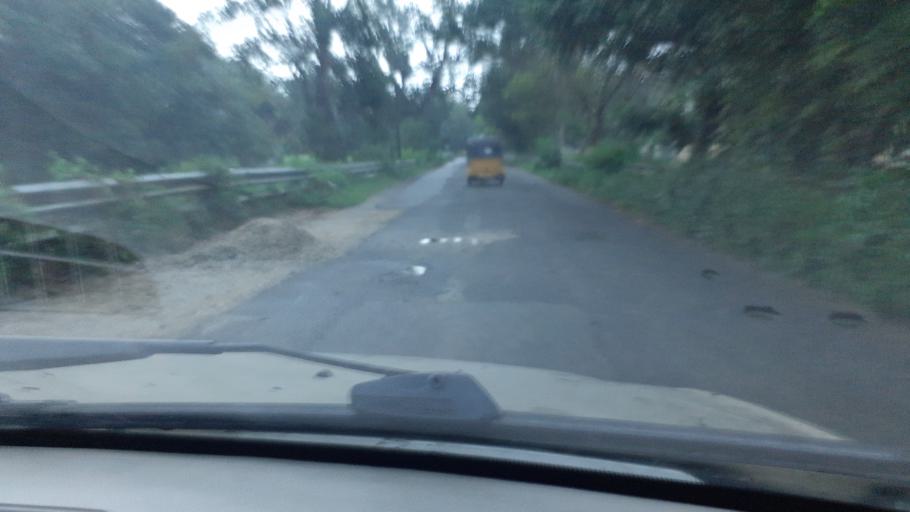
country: IN
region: Tamil Nadu
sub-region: Kanniyakumari
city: Padmanabhapuram
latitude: 8.3625
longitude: 77.3143
